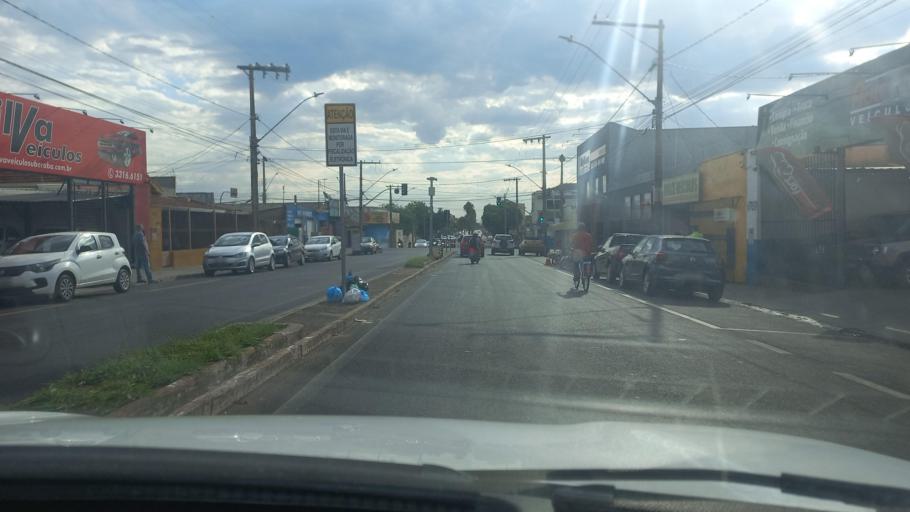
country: BR
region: Minas Gerais
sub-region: Uberaba
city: Uberaba
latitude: -19.7681
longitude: -47.9239
